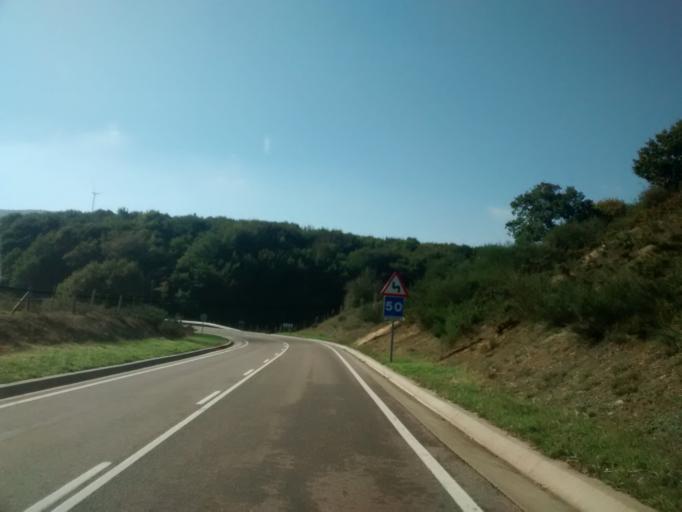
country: ES
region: Cantabria
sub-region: Provincia de Cantabria
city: Reinosa
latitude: 42.9804
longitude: -4.1042
